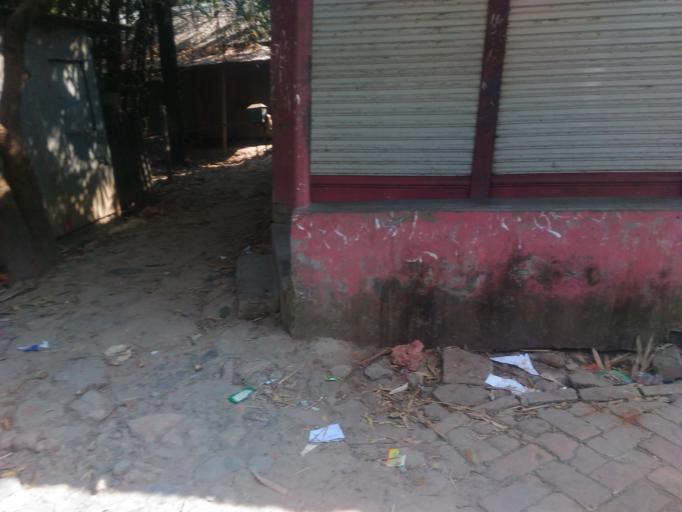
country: BD
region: Dhaka
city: Tungi
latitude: 24.0103
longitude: 90.3805
